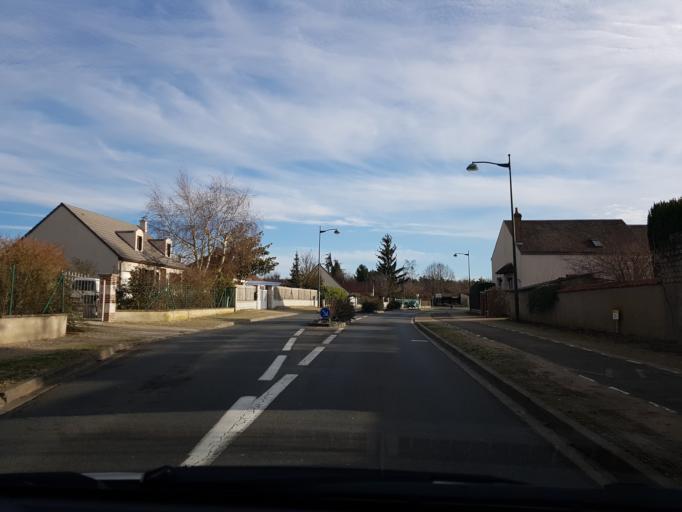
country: FR
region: Centre
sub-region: Departement du Loiret
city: Jargeau
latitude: 47.8574
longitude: 2.1283
